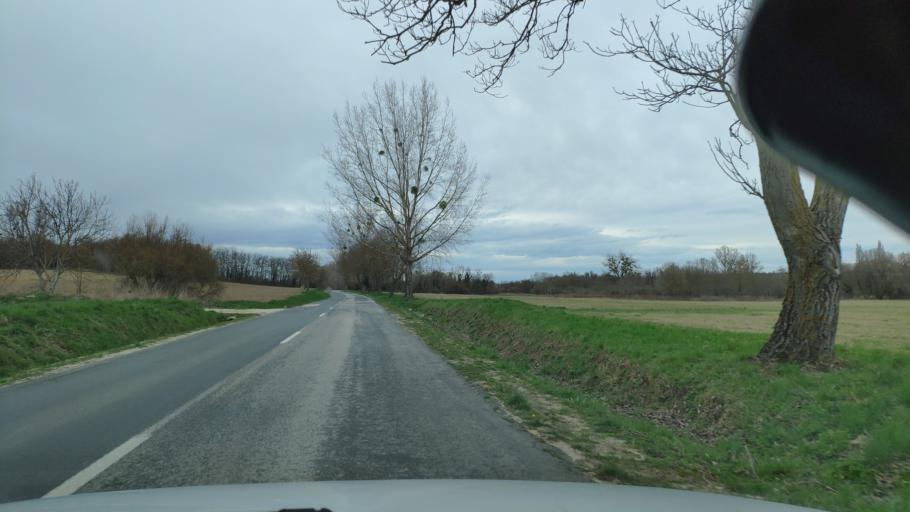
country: HU
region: Zala
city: Sarmellek
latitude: 46.6654
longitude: 17.1132
